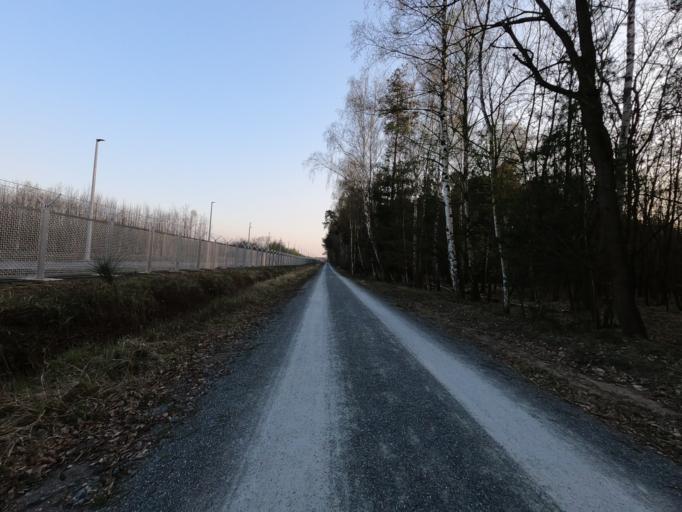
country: DE
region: Hesse
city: Kelsterbach
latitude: 50.0097
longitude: 8.5221
